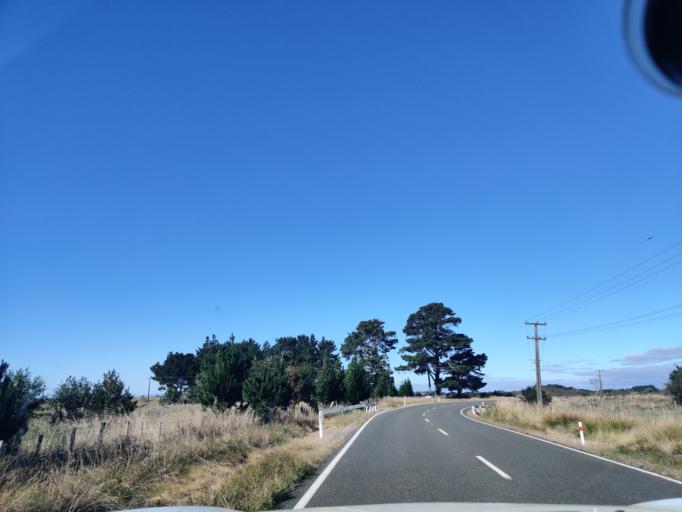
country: NZ
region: Manawatu-Wanganui
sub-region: Horowhenua District
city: Foxton
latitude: -40.3824
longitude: 175.2712
